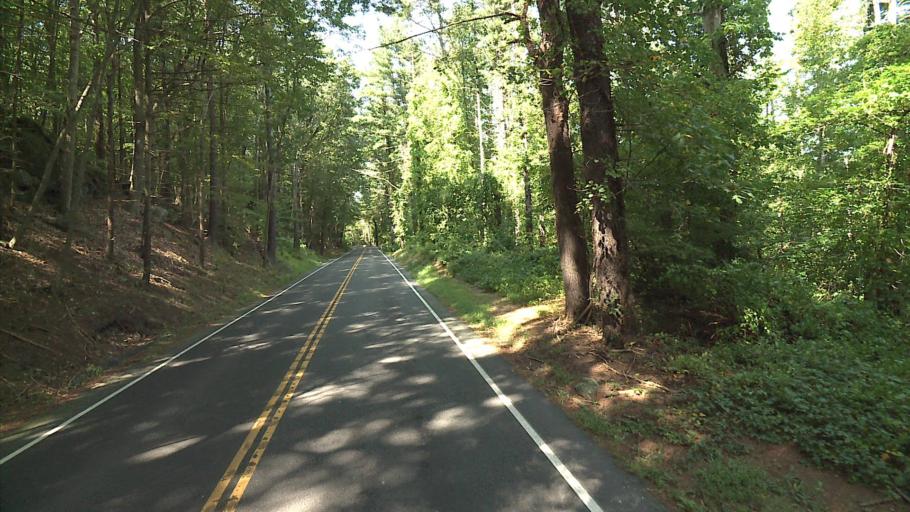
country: US
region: Connecticut
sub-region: Fairfield County
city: Southport
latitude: 41.2194
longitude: -73.2980
